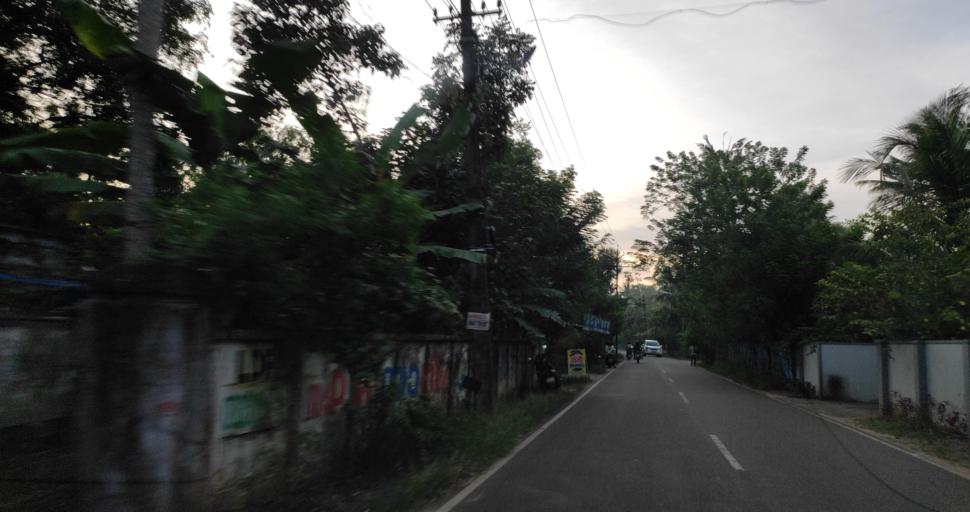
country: IN
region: Kerala
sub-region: Alappuzha
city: Shertallai
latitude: 9.6368
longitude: 76.3660
